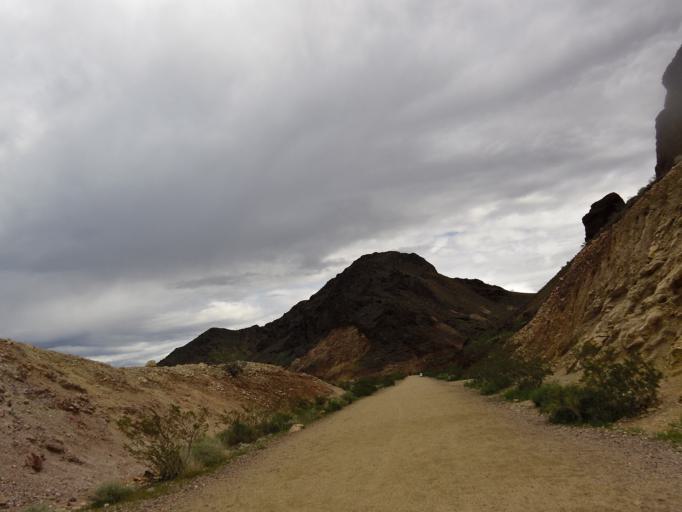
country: US
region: Nevada
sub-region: Clark County
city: Boulder City
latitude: 36.0132
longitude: -114.7862
